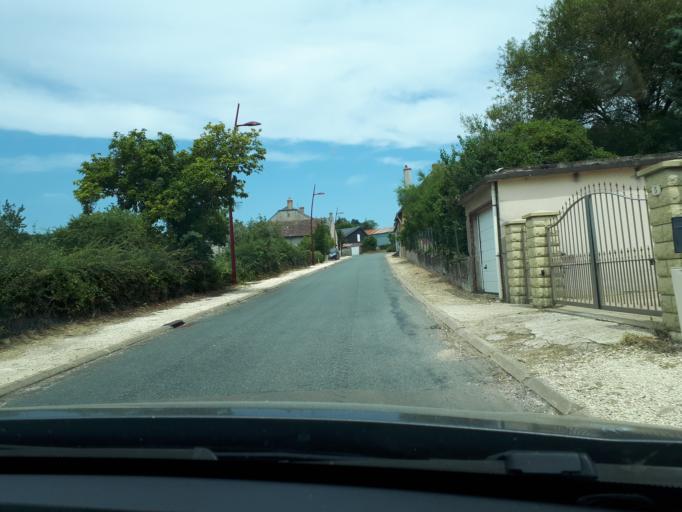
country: FR
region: Centre
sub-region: Departement du Cher
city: Sancerre
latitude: 47.3036
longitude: 2.7455
